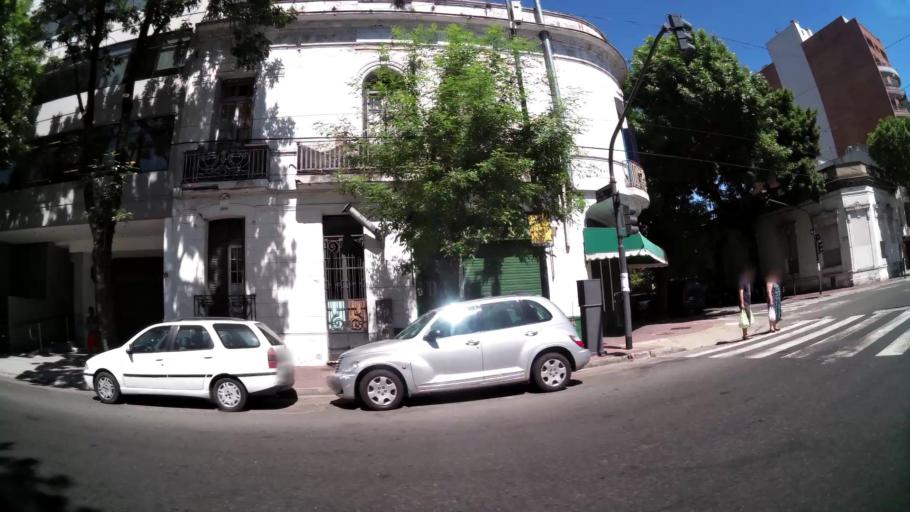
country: AR
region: Buenos Aires F.D.
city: Buenos Aires
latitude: -34.6338
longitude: -58.3996
